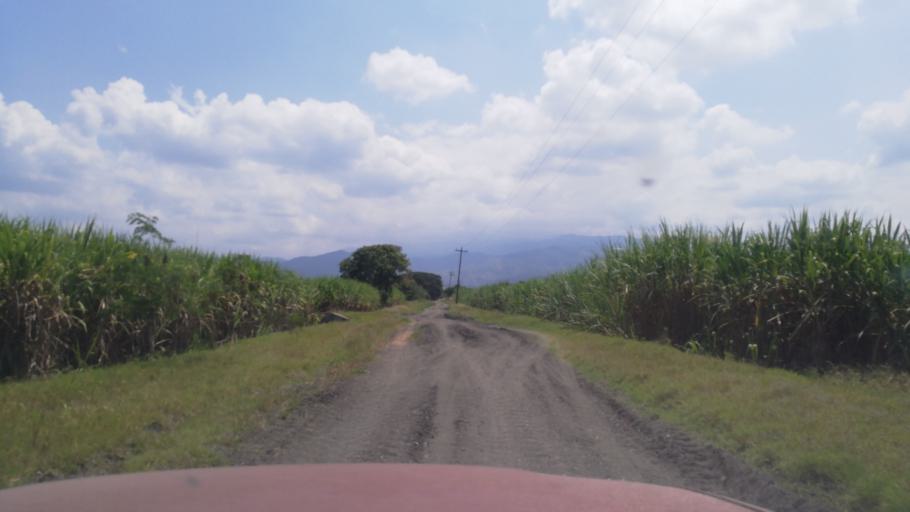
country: CO
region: Valle del Cauca
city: San Pedro
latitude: 3.9941
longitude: -76.2686
